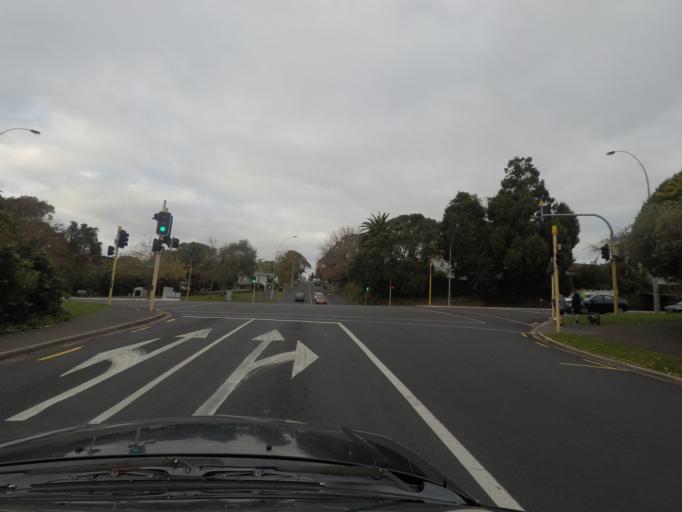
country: NZ
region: Auckland
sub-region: Auckland
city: Auckland
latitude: -36.8908
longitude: 174.7662
